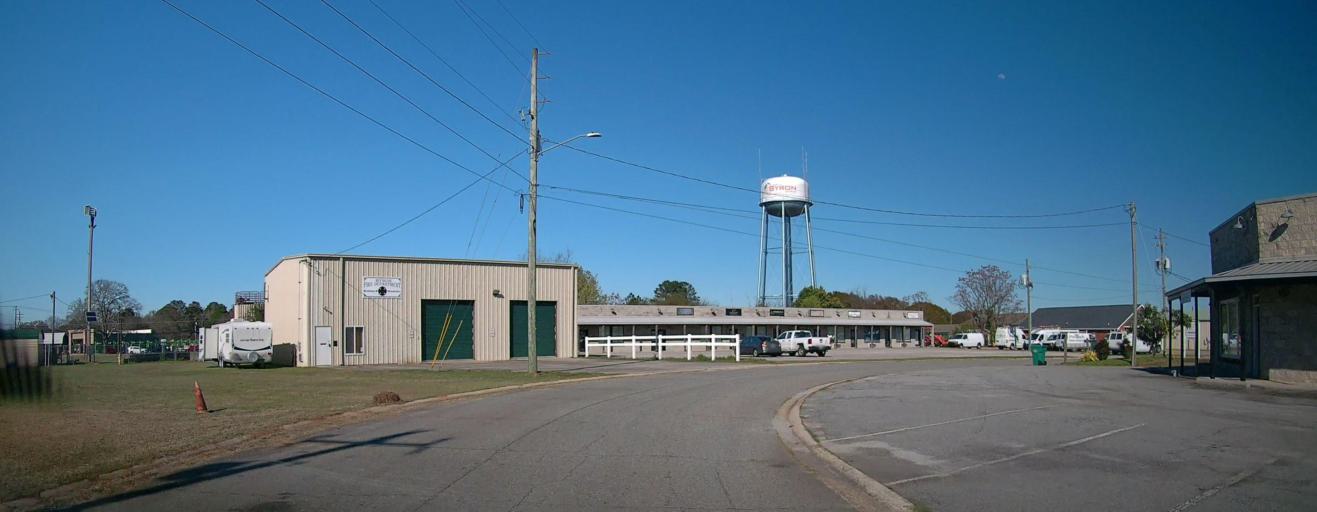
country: US
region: Georgia
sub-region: Peach County
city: Byron
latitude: 32.6499
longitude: -83.7559
